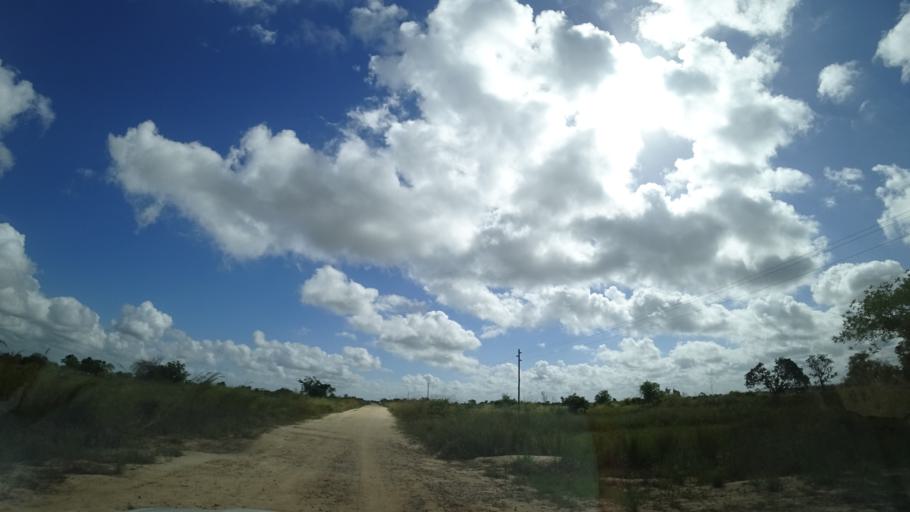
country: MZ
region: Sofala
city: Dondo
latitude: -19.4441
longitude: 34.5620
